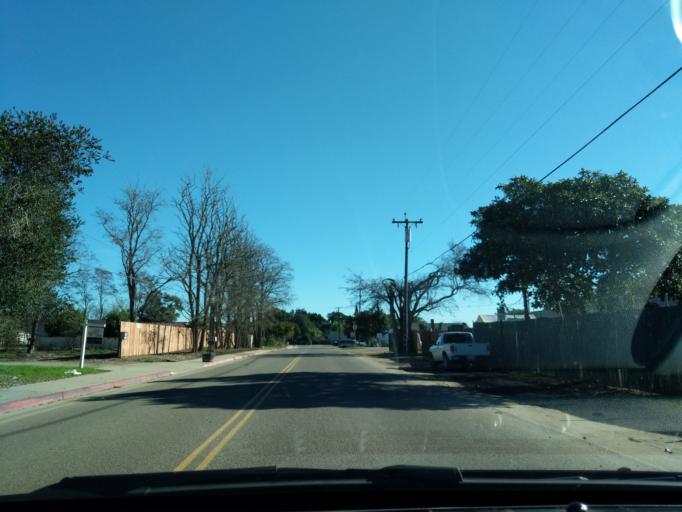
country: US
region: California
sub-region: San Luis Obispo County
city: Nipomo
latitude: 35.0341
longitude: -120.4790
